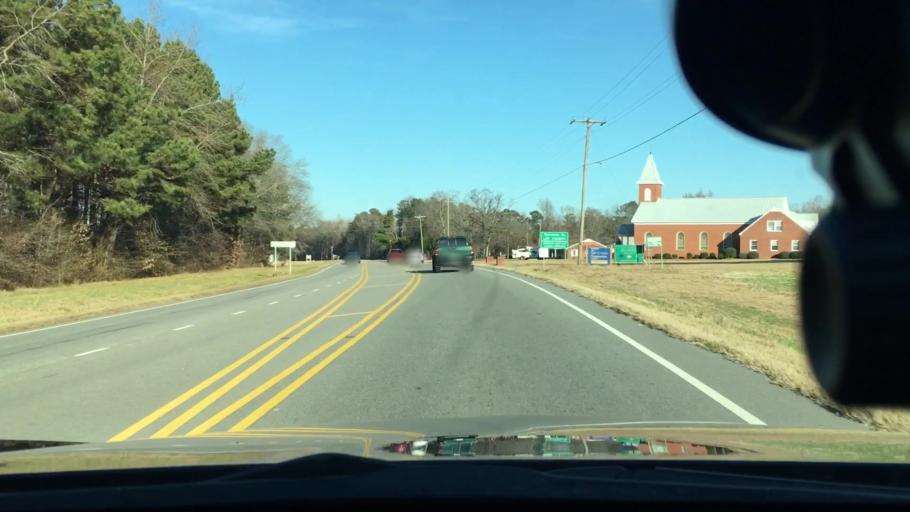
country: US
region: North Carolina
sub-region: Lee County
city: Sanford
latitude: 35.3817
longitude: -79.2796
